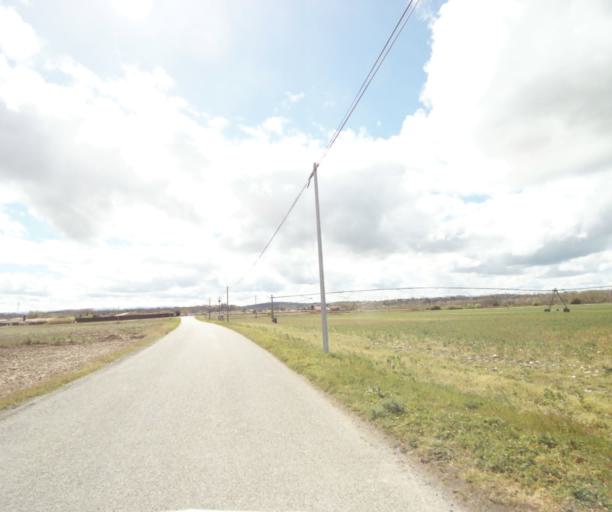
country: FR
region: Midi-Pyrenees
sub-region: Departement de l'Ariege
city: Saverdun
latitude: 43.2425
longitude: 1.5868
